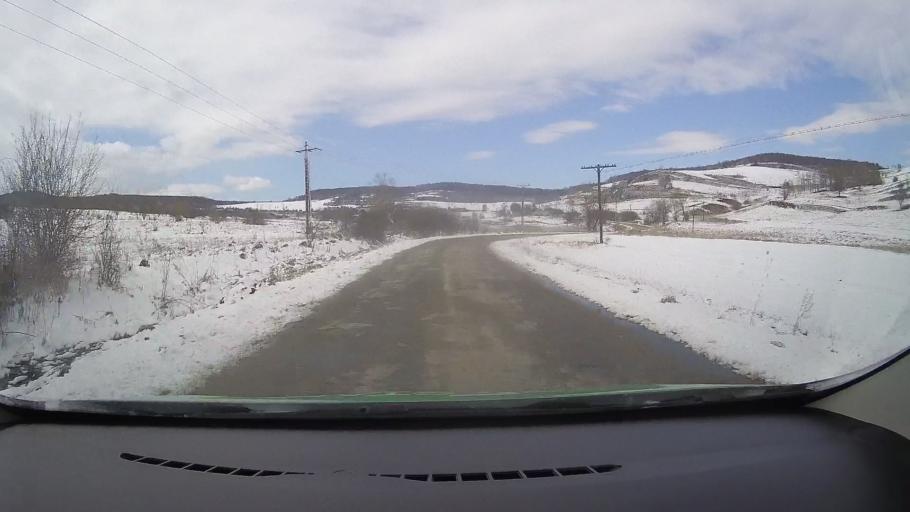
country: RO
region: Sibiu
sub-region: Comuna Altina
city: Altina
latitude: 45.9899
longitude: 24.4476
